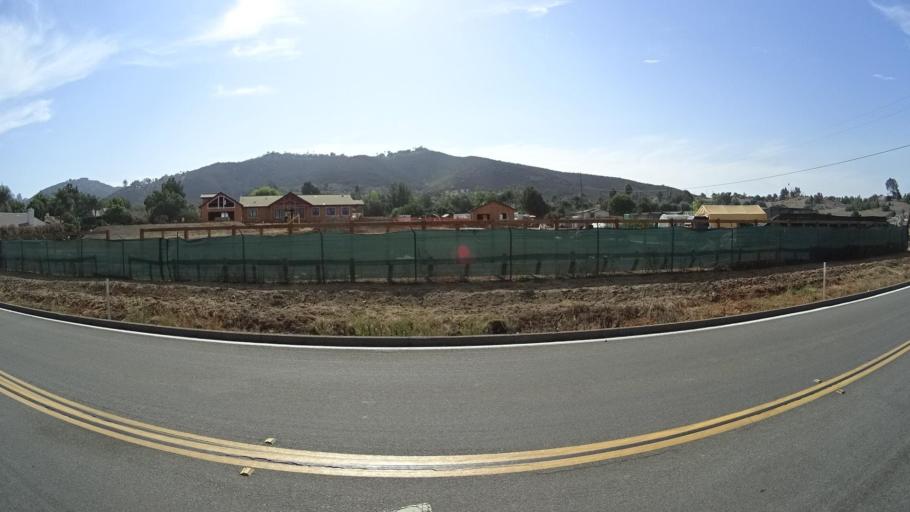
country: US
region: California
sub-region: San Diego County
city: San Marcos
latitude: 33.1715
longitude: -117.1496
